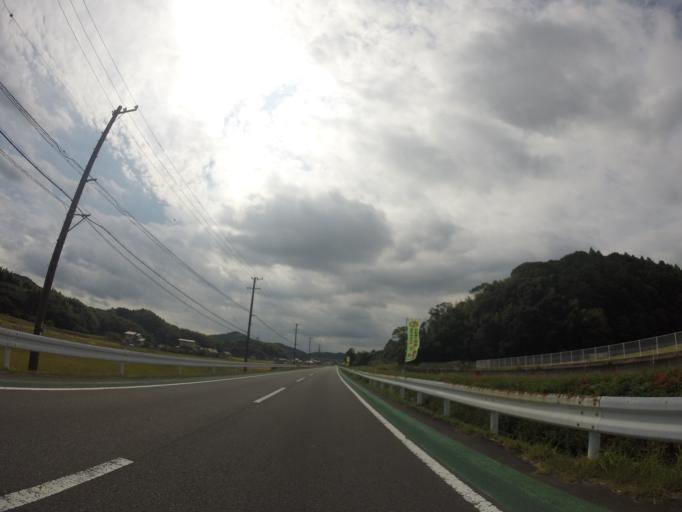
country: JP
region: Shizuoka
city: Shimada
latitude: 34.8629
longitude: 138.1827
